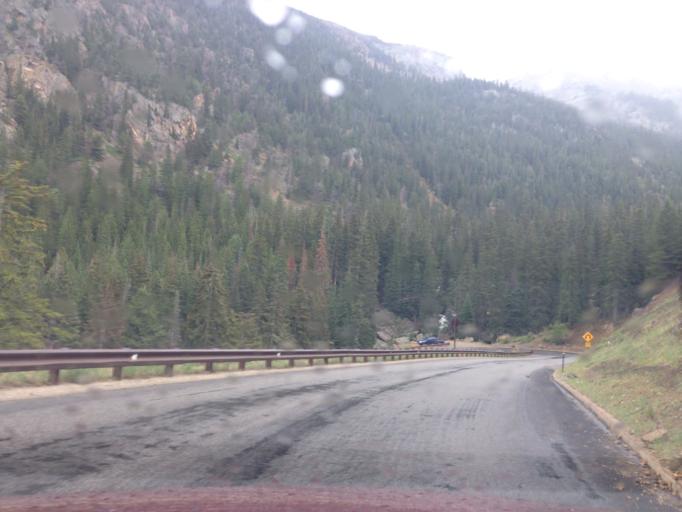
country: US
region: Colorado
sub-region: Clear Creek County
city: Georgetown
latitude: 39.6775
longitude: -105.7005
